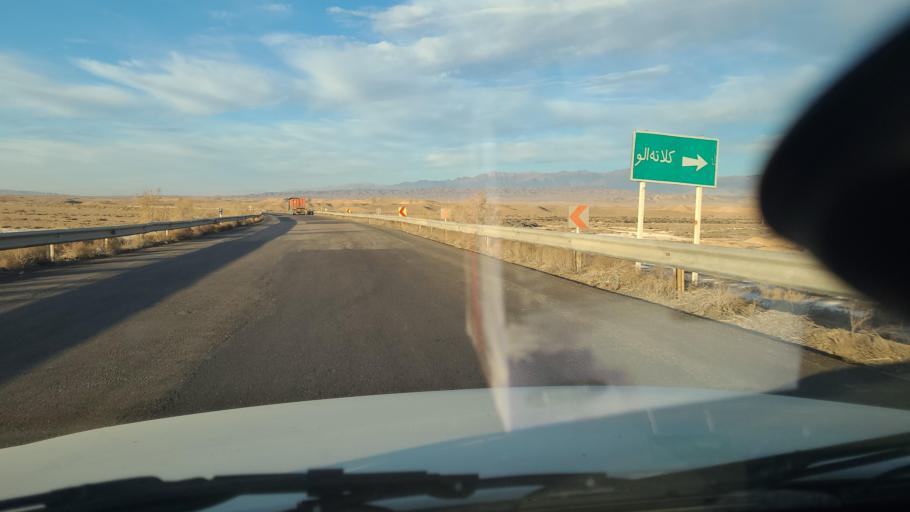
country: IR
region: Razavi Khorasan
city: Neqab
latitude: 36.7839
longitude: 57.5893
